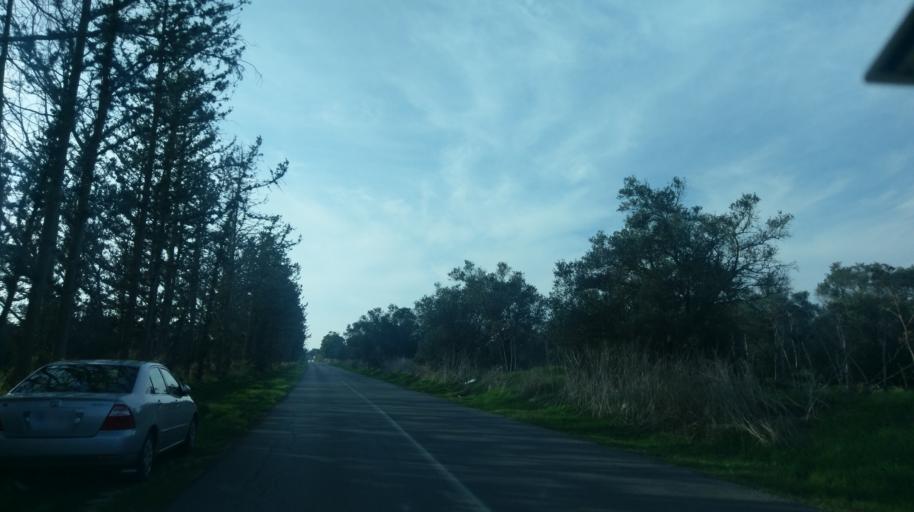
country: CY
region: Ammochostos
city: Achna
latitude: 35.1070
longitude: 33.7587
